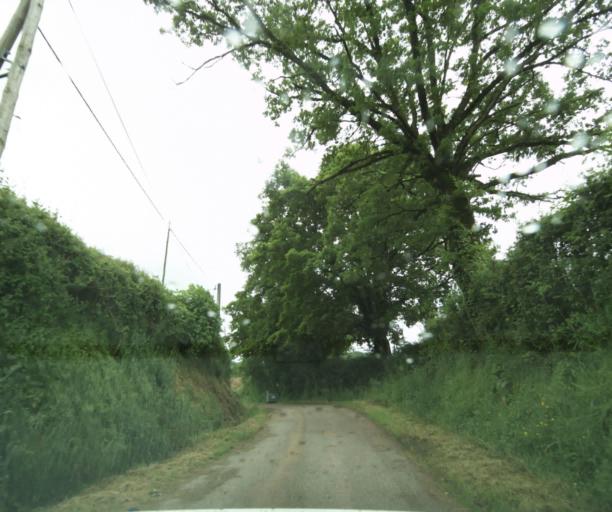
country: FR
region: Bourgogne
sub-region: Departement de Saone-et-Loire
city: Charolles
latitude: 46.4400
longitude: 4.4250
